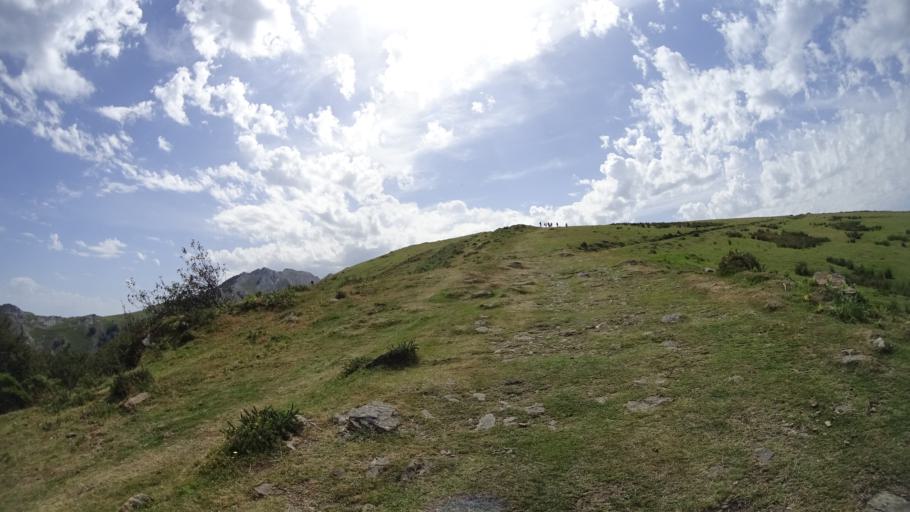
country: ES
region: Basque Country
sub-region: Bizkaia
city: Manaria
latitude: 43.0954
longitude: -2.6312
